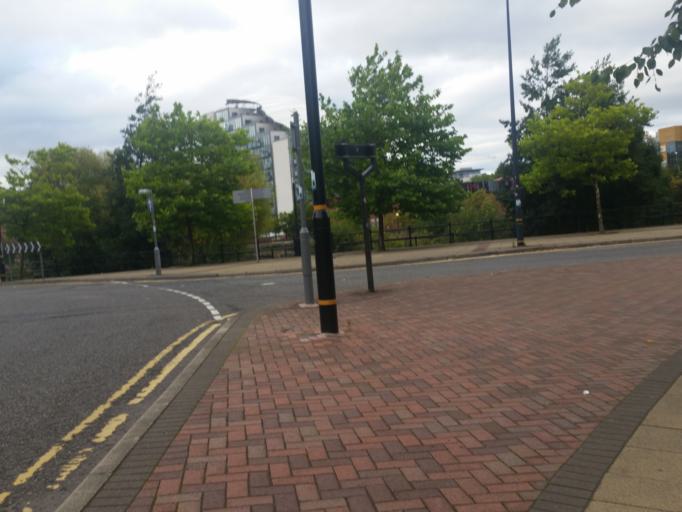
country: GB
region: England
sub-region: City and Borough of Salford
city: Salford
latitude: 53.4654
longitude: -2.2863
